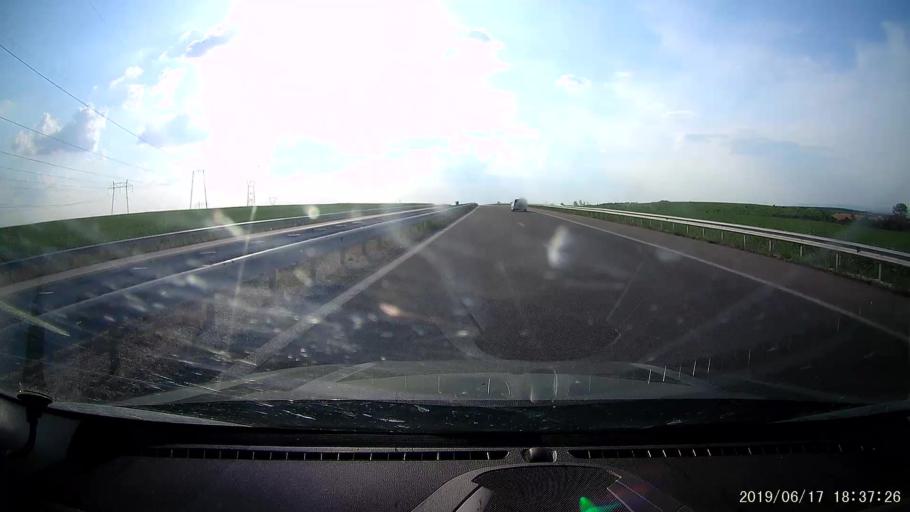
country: BG
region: Stara Zagora
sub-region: Obshtina Chirpan
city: Chirpan
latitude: 42.1302
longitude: 25.3612
